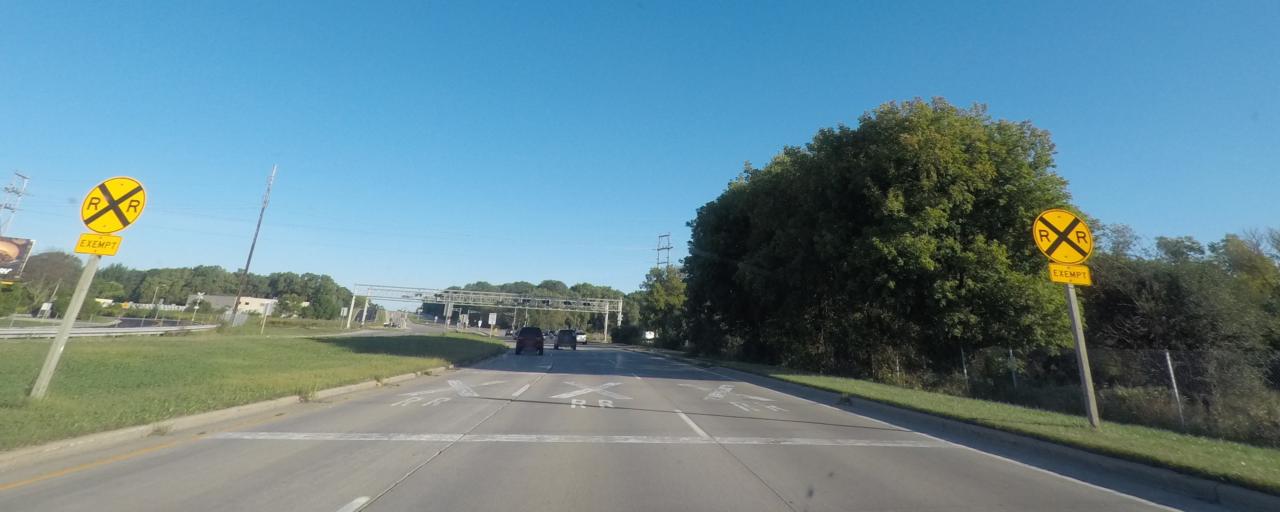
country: US
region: Wisconsin
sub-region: Dane County
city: Monona
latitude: 43.1091
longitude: -89.3167
